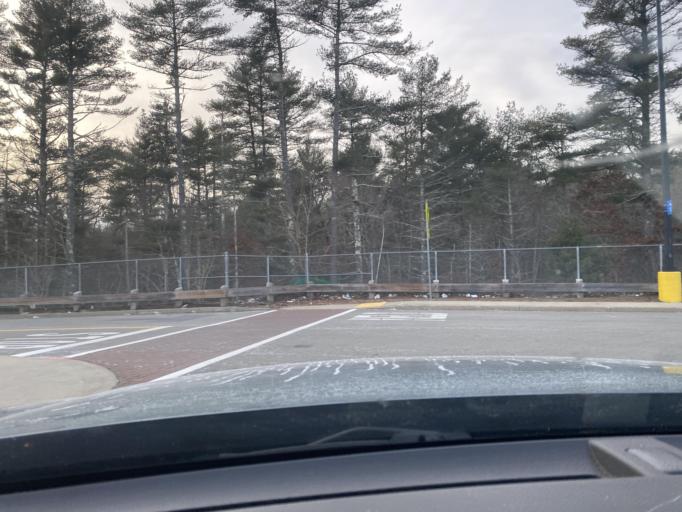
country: US
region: Massachusetts
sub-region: Plymouth County
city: West Wareham
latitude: 41.7798
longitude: -70.7472
